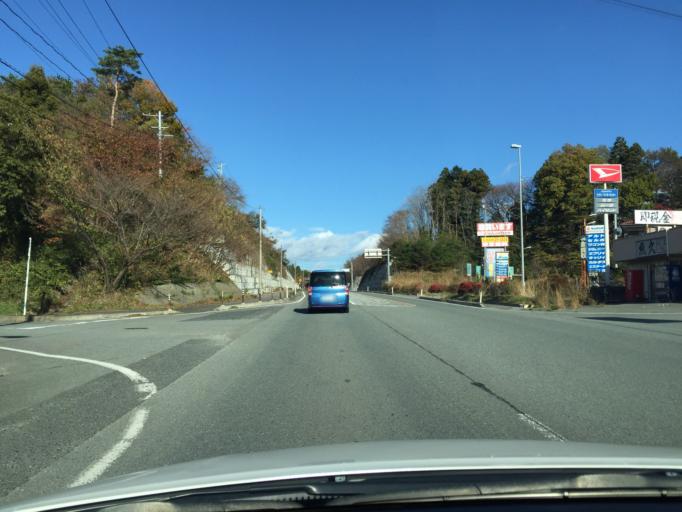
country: JP
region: Fukushima
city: Namie
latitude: 37.2835
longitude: 140.9919
